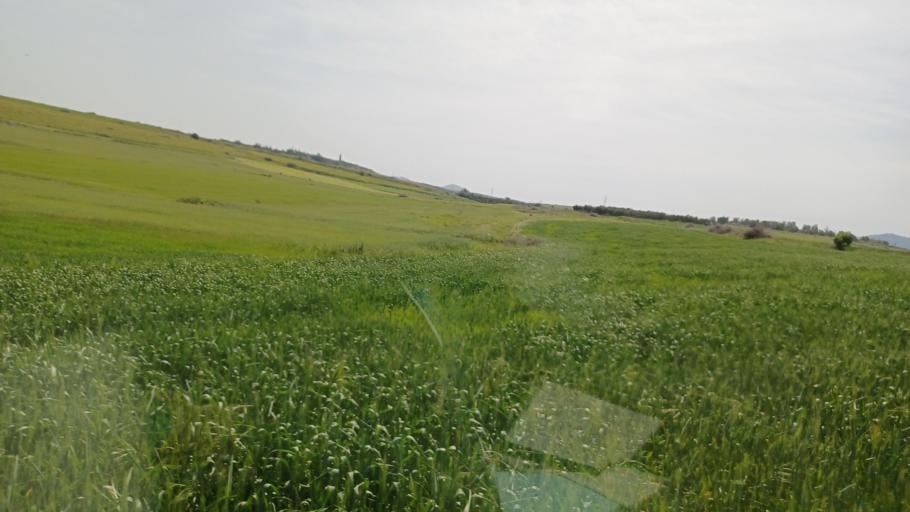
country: CY
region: Lefkosia
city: Astromeritis
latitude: 35.1003
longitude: 32.9608
